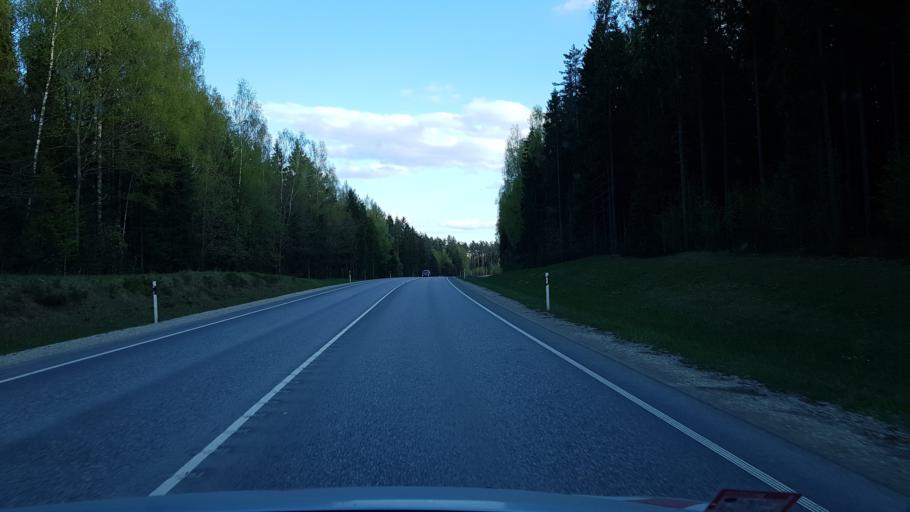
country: EE
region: Vorumaa
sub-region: Voru linn
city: Voru
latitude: 57.9675
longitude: 26.7885
